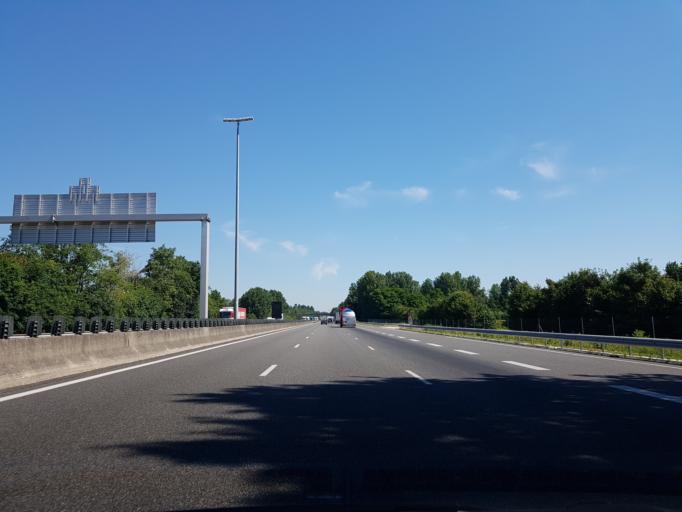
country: FR
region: Picardie
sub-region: Departement de l'Oise
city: Chevrieres
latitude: 49.3228
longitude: 2.6884
